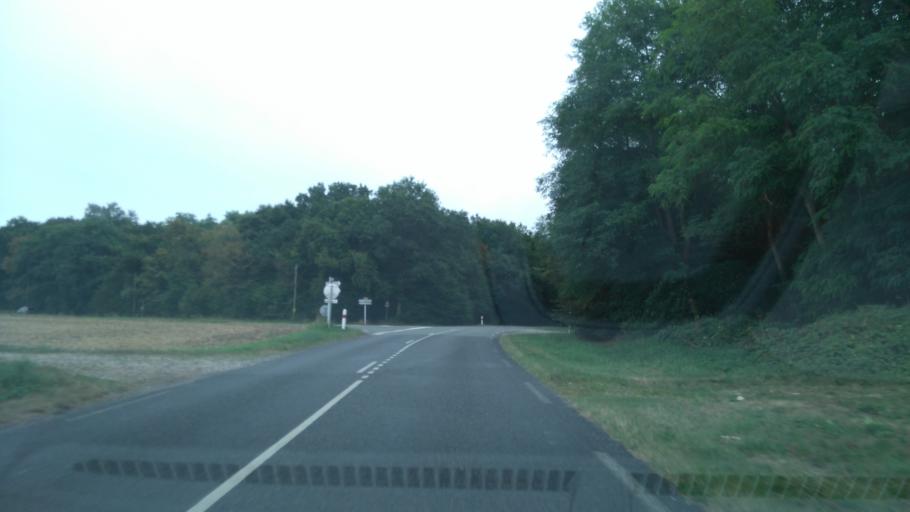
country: FR
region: Picardie
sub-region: Departement de l'Oise
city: Precy-sur-Oise
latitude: 49.1922
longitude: 2.3847
